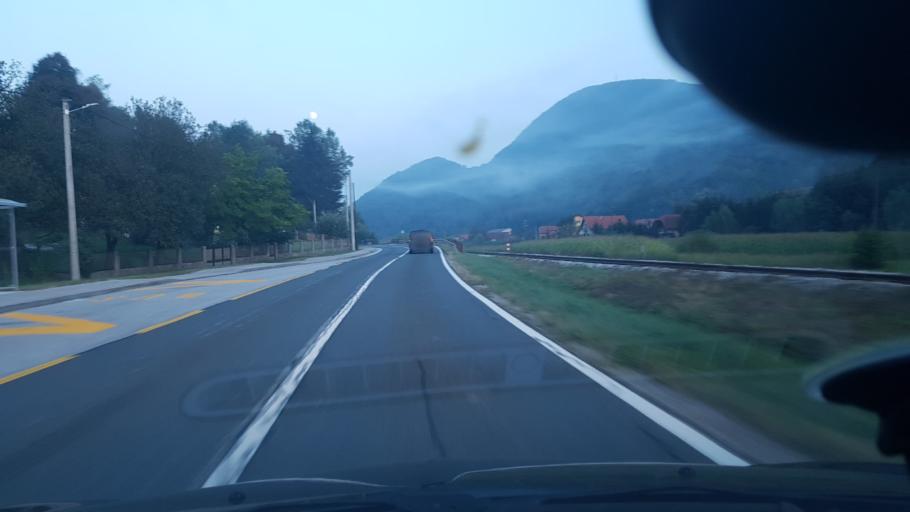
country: HR
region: Krapinsko-Zagorska
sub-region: Grad Krapina
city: Krapina
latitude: 46.2014
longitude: 15.8290
